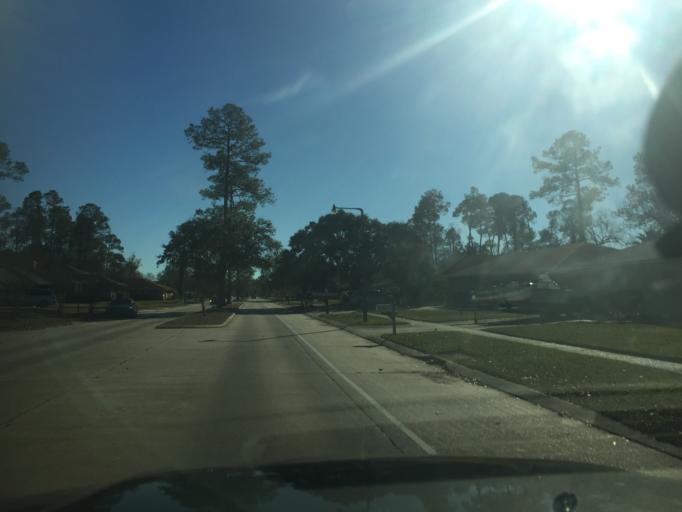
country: US
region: Louisiana
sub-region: Saint Tammany Parish
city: Slidell
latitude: 30.2899
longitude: -89.7585
